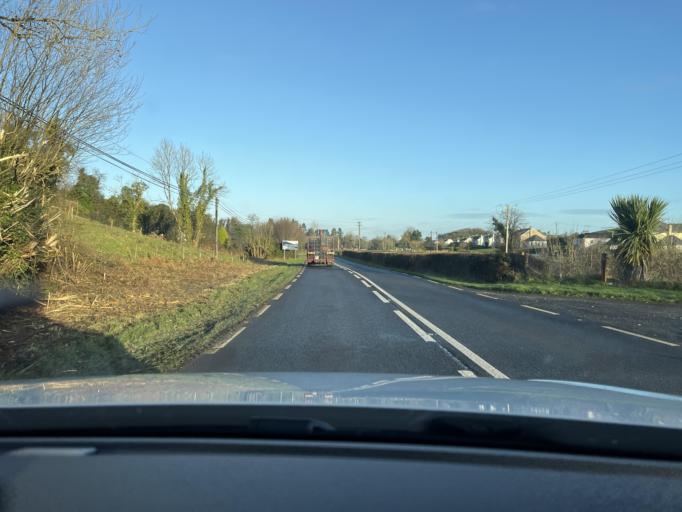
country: IE
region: Ulster
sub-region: An Cabhan
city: Ballyconnell
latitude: 54.1170
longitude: -7.6074
